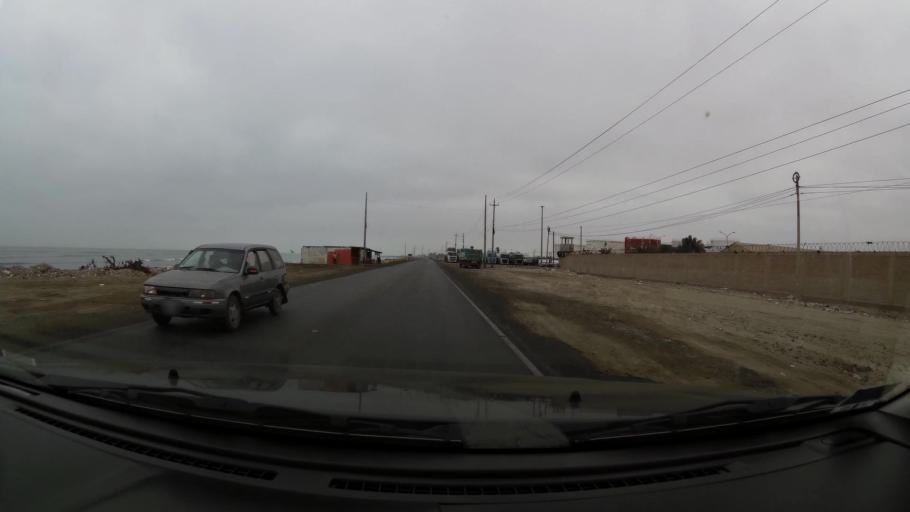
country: PE
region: Ica
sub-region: Provincia de Pisco
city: Pisco
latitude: -13.7488
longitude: -76.2290
